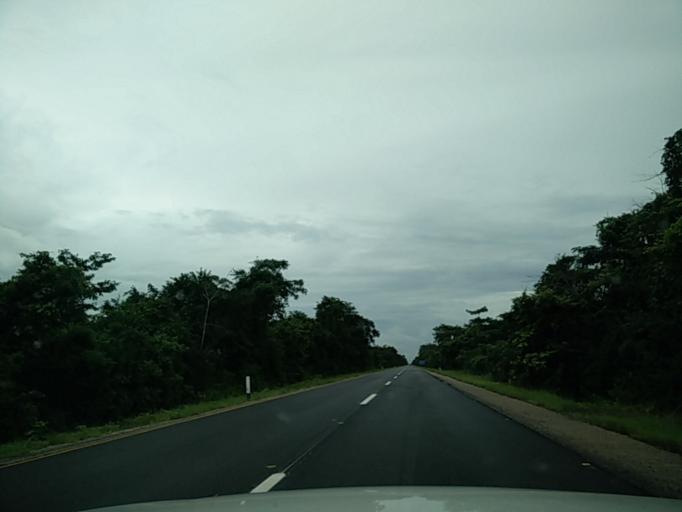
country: MX
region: Quintana Roo
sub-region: Lazaro Cardenas
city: Nuevo Xcan
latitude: 20.8804
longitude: -87.5935
